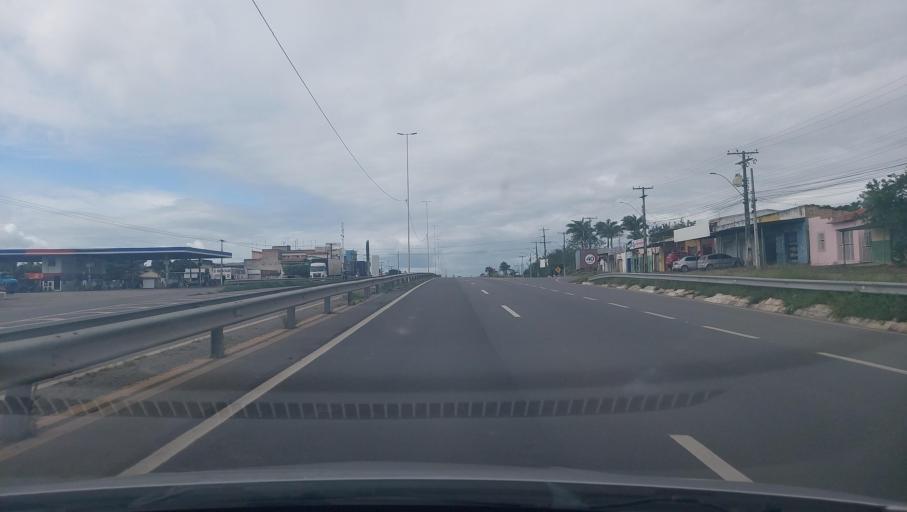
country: BR
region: Bahia
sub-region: Santo Estevao
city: Santo Estevao
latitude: -12.4498
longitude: -39.2485
